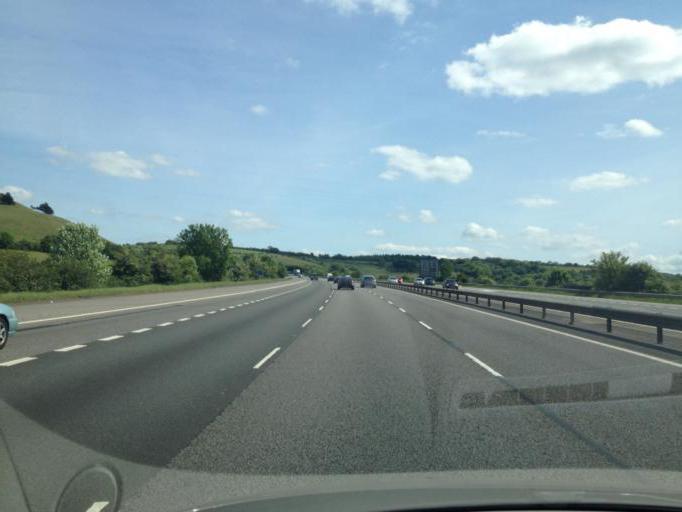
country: GB
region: England
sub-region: Oxfordshire
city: Watlington
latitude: 51.6701
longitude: -0.9589
